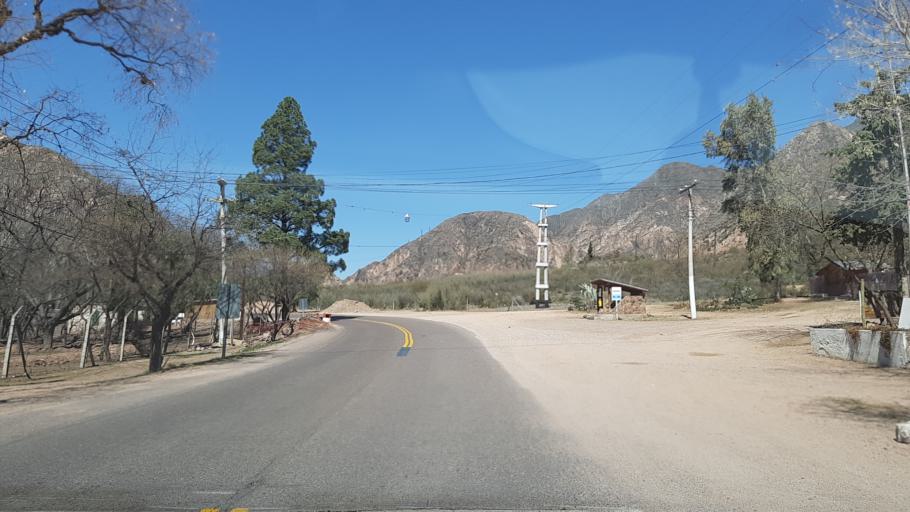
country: AR
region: Mendoza
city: Lujan de Cuyo
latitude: -33.0190
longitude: -69.1168
